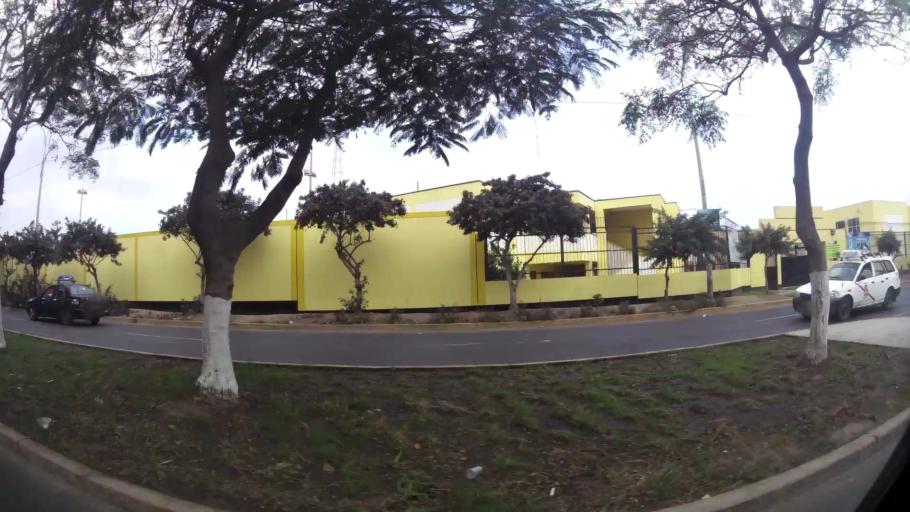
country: PE
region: La Libertad
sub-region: Provincia de Trujillo
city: Trujillo
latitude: -8.1033
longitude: -79.0287
